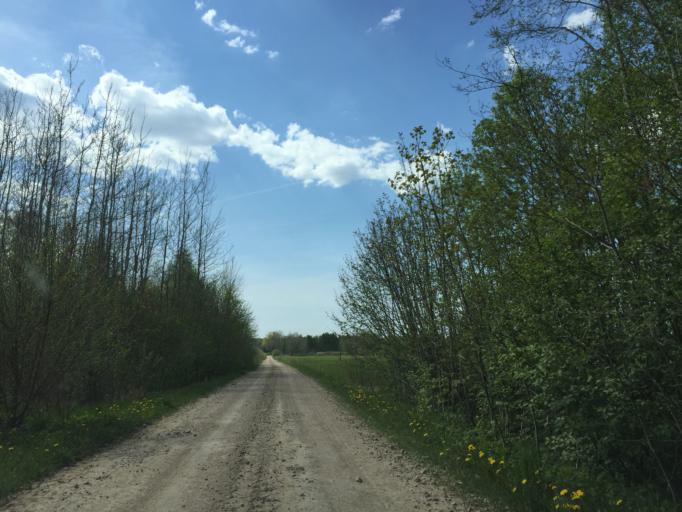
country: LV
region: Limbazu Rajons
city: Limbazi
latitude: 57.3803
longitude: 24.6464
